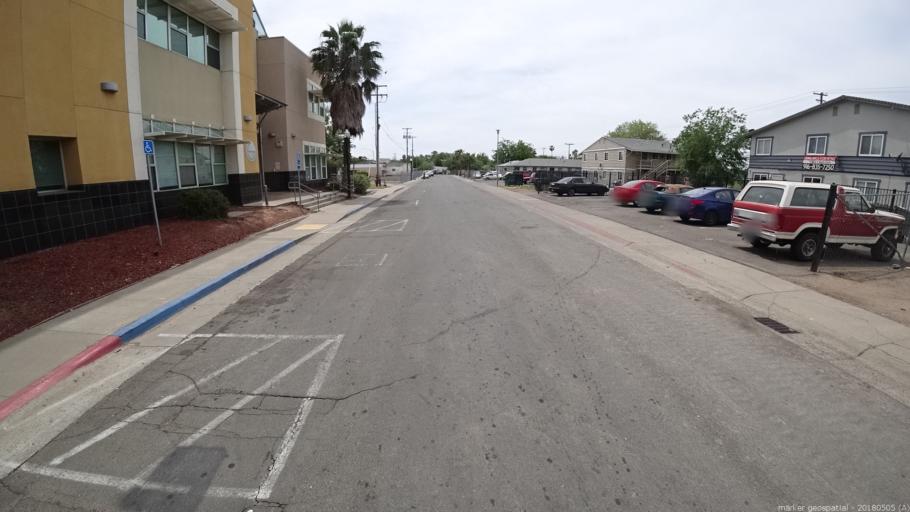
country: US
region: California
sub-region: Sacramento County
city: Rio Linda
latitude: 38.6360
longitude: -121.4307
